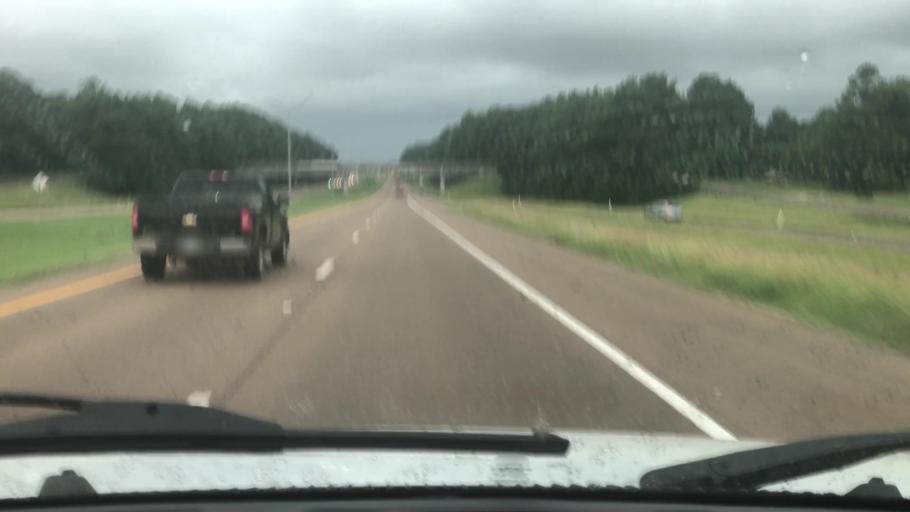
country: US
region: Texas
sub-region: Bowie County
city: Wake Village
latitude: 33.4170
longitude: -94.0969
